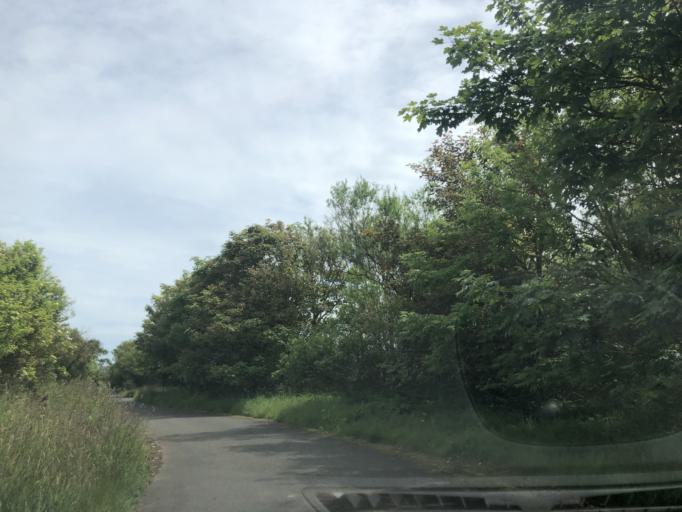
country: GB
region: Scotland
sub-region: Fife
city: Anstruther
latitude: 56.2720
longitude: -2.5999
